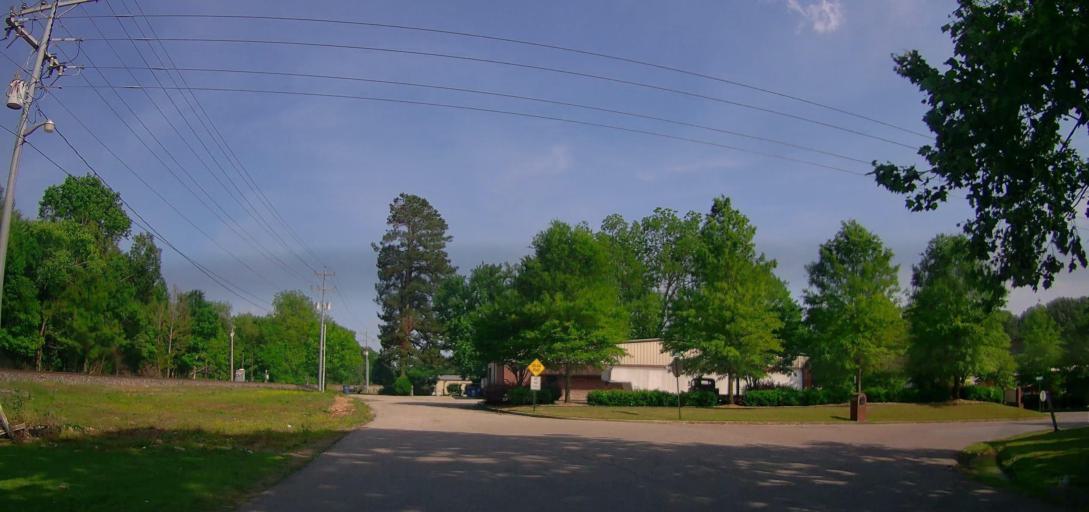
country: US
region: Mississippi
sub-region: De Soto County
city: Olive Branch
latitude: 34.9902
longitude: -89.8610
